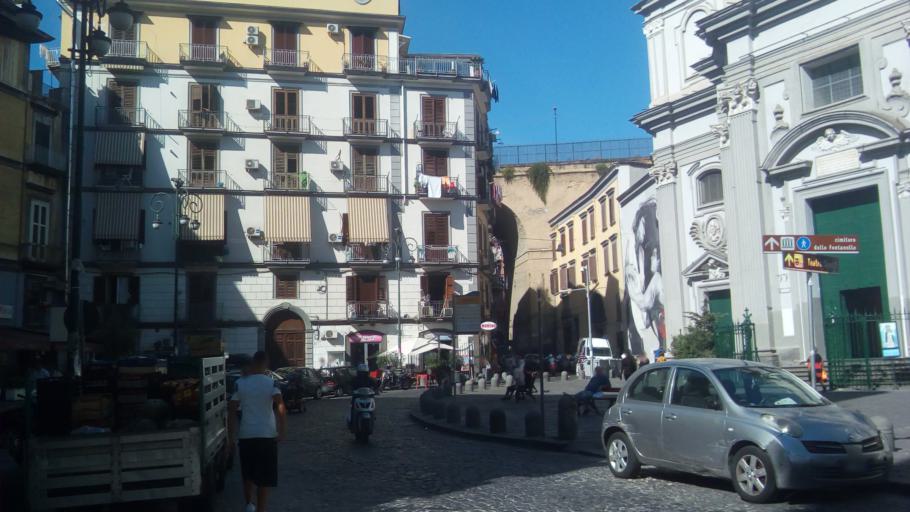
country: IT
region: Campania
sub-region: Provincia di Napoli
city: Napoli
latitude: 40.8596
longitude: 14.2506
